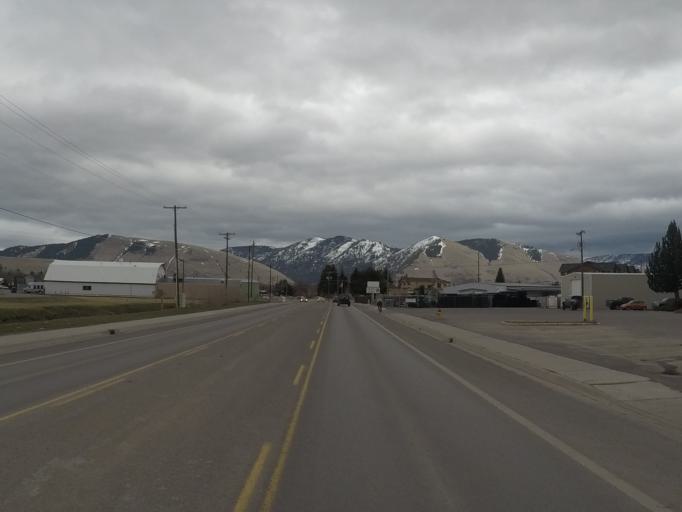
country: US
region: Montana
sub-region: Missoula County
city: Orchard Homes
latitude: 46.8813
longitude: -114.0261
